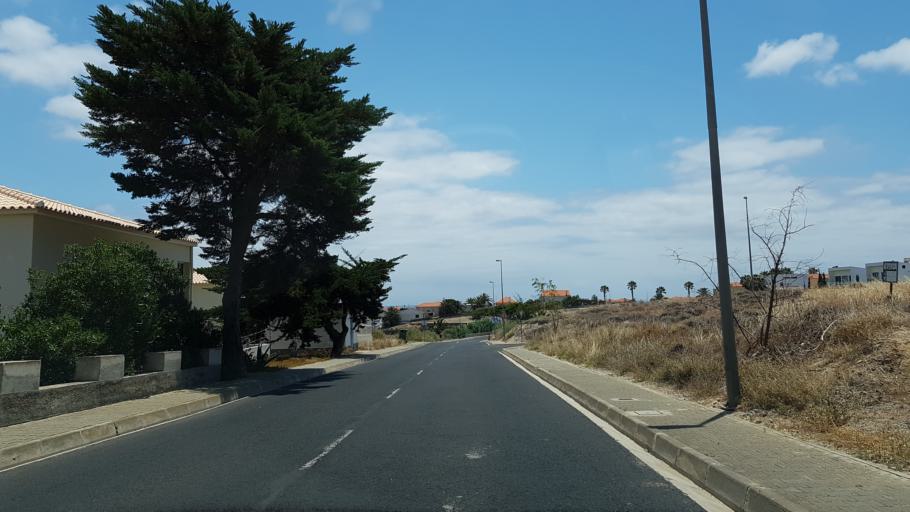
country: PT
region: Madeira
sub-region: Porto Santo
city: Vila de Porto Santo
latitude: 33.0594
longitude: -16.3424
